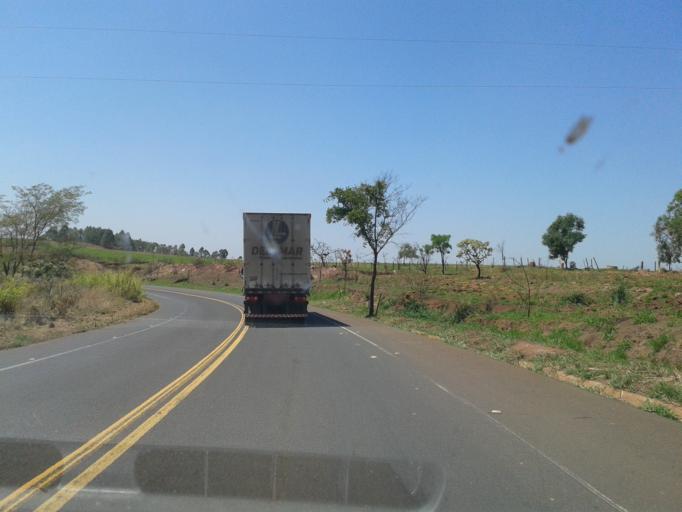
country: BR
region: Minas Gerais
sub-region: Araxa
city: Araxa
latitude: -19.4239
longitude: -47.2456
